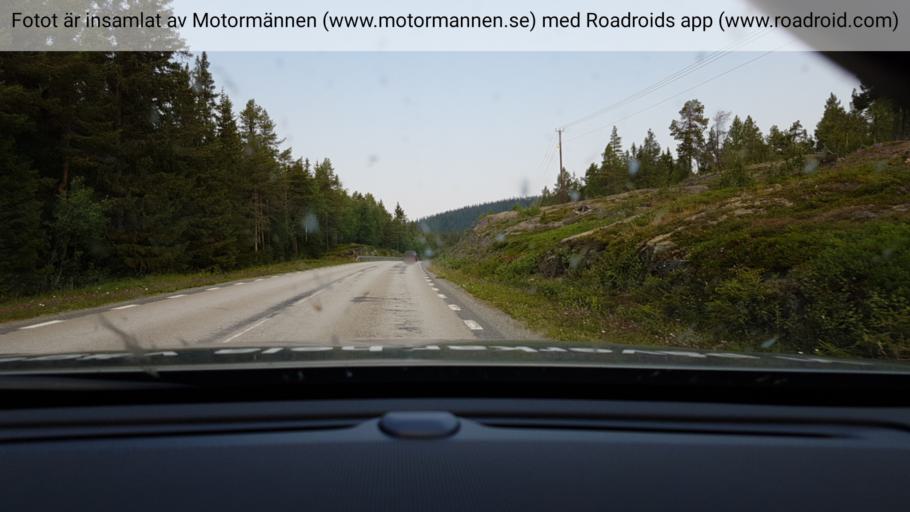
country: SE
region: Vaesterbotten
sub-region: Vilhelmina Kommun
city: Sjoberg
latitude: 65.5421
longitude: 15.5817
